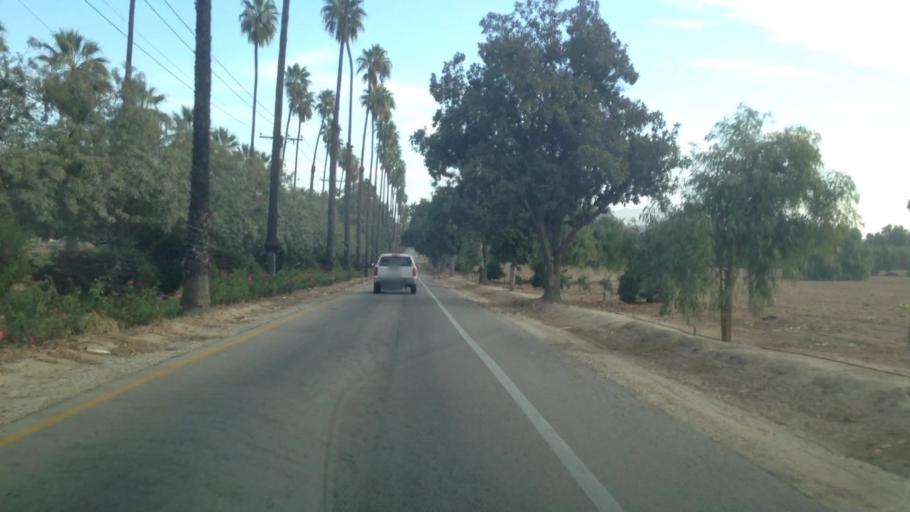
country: US
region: California
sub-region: Riverside County
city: Riverside
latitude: 33.9263
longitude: -117.3957
